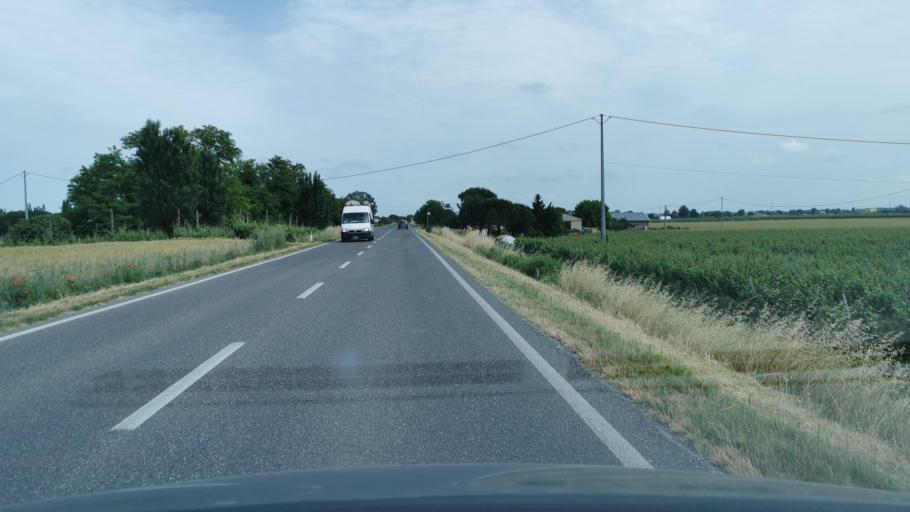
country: IT
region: Emilia-Romagna
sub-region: Provincia di Ravenna
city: Sant'Alberto
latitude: 44.5399
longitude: 12.1480
